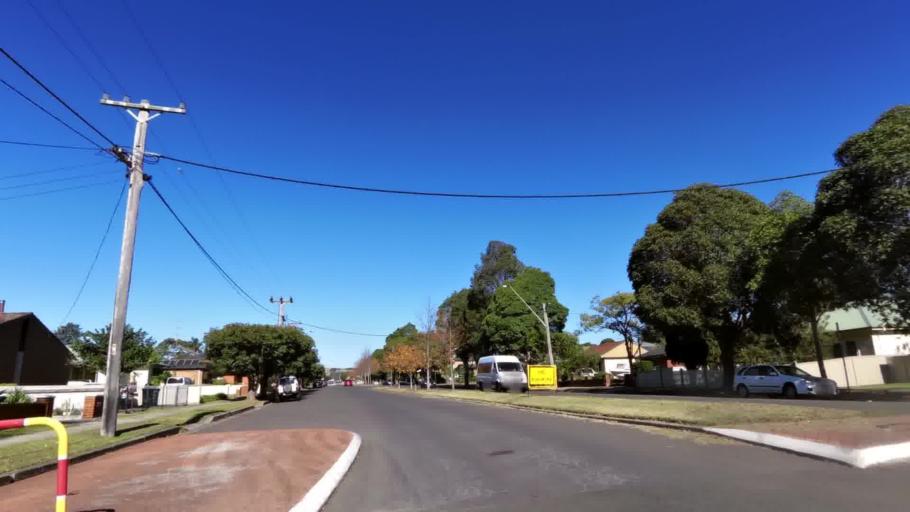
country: AU
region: New South Wales
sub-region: Shellharbour
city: Albion Park Rail
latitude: -34.5591
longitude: 150.8186
